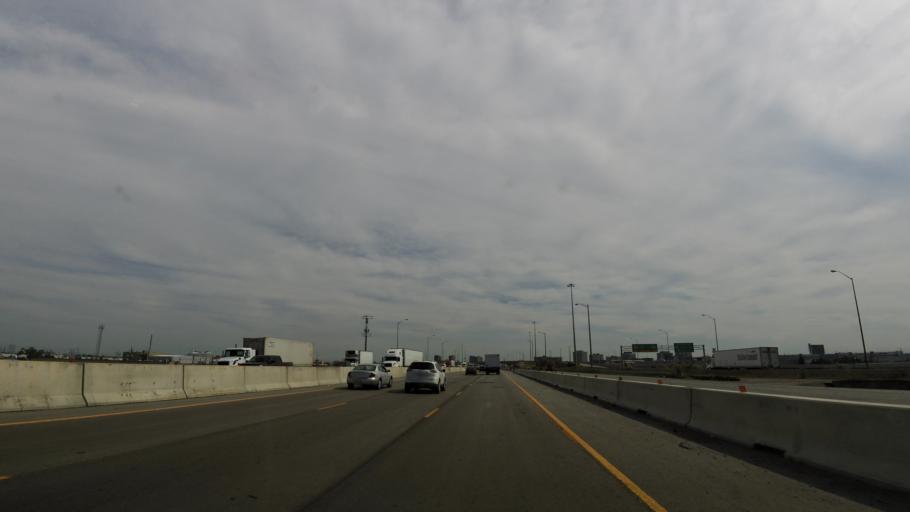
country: CA
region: Ontario
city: Etobicoke
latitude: 43.7040
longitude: -79.6116
